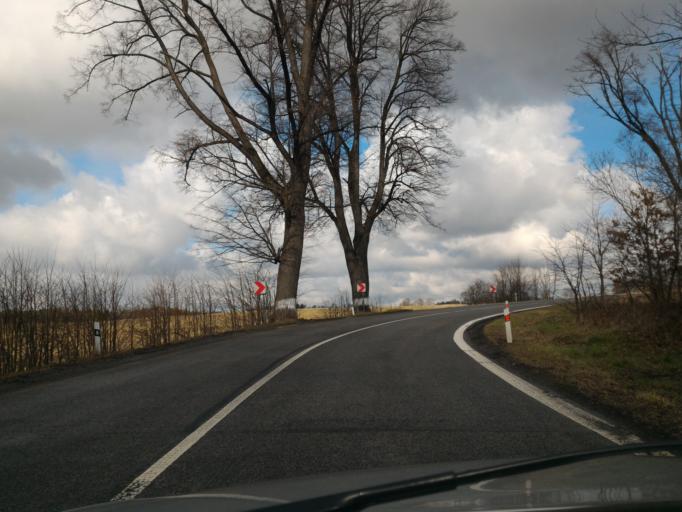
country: PL
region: Silesian Voivodeship
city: Zawidow
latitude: 50.9842
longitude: 15.0746
